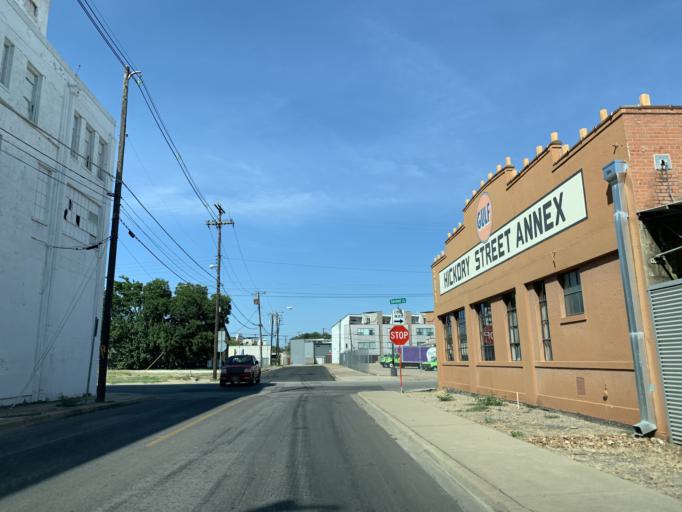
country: US
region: Texas
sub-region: Dallas County
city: Dallas
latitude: 32.7823
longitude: -96.7731
